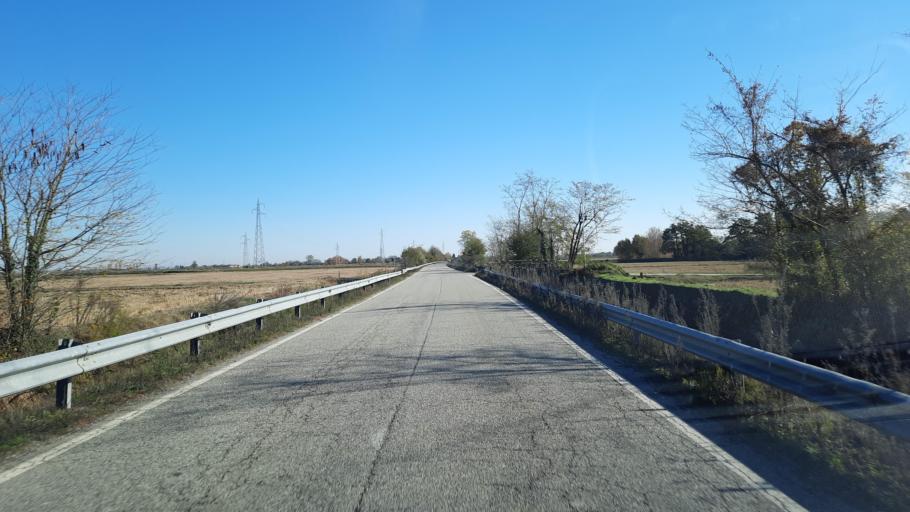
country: IT
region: Piedmont
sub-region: Provincia di Alessandria
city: Balzola
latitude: 45.1879
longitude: 8.4090
